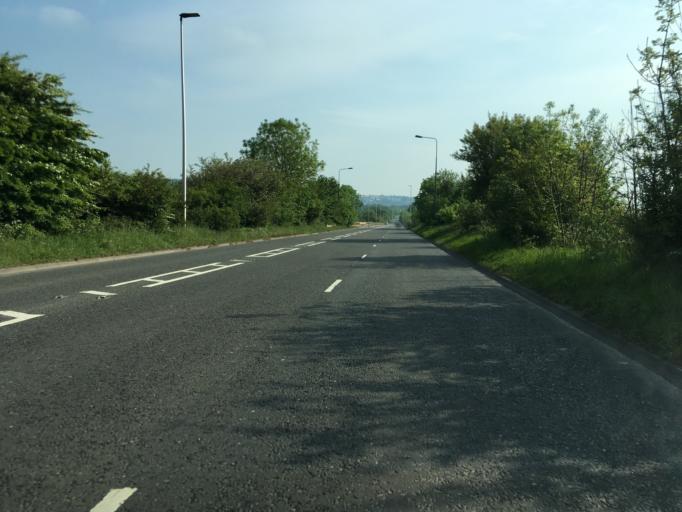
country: GB
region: England
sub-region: North Somerset
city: Long Ashton
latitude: 51.4260
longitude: -2.6518
